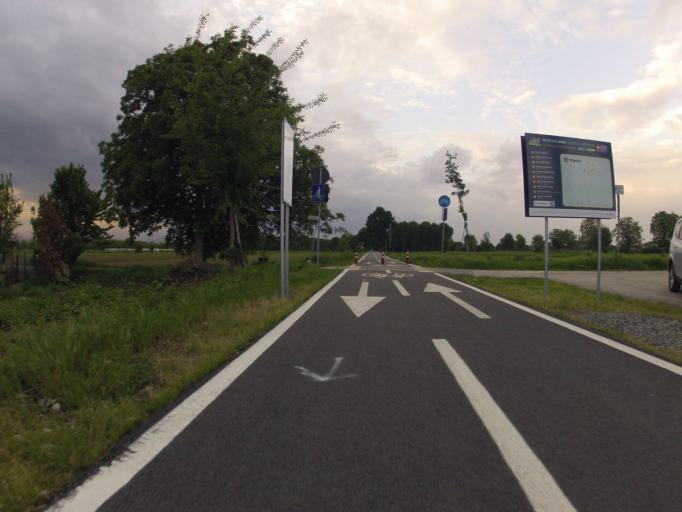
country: IT
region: Piedmont
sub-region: Provincia di Torino
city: Vigone
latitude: 44.8472
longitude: 7.4912
